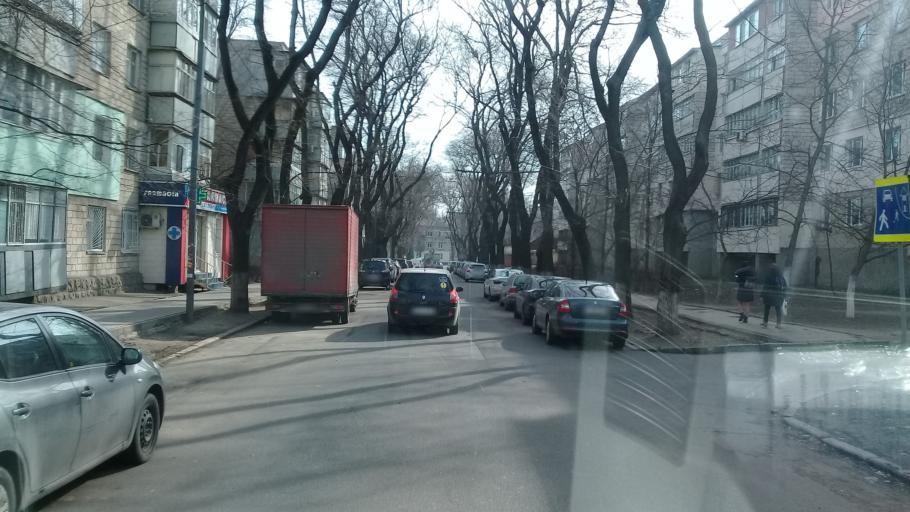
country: MD
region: Chisinau
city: Chisinau
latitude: 47.0022
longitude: 28.8191
